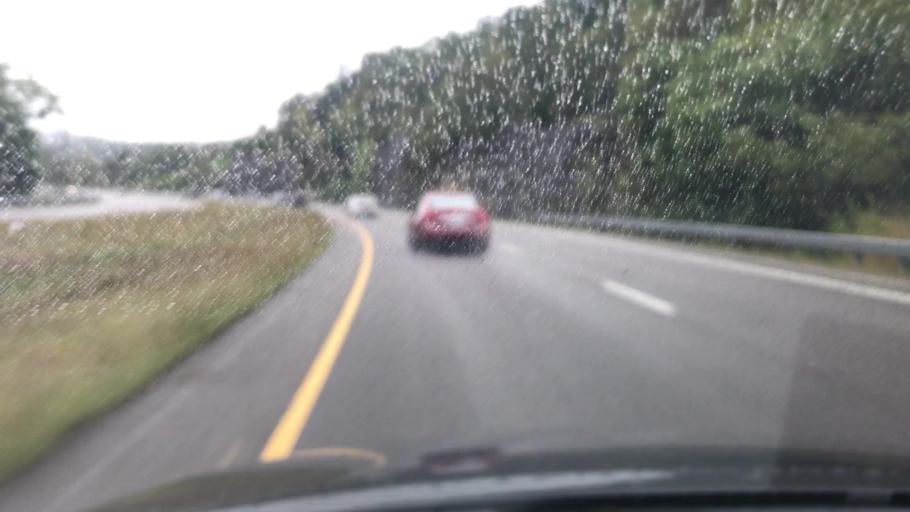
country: US
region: Tennessee
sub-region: Cheatham County
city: Ashland City
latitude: 36.2216
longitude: -86.9697
